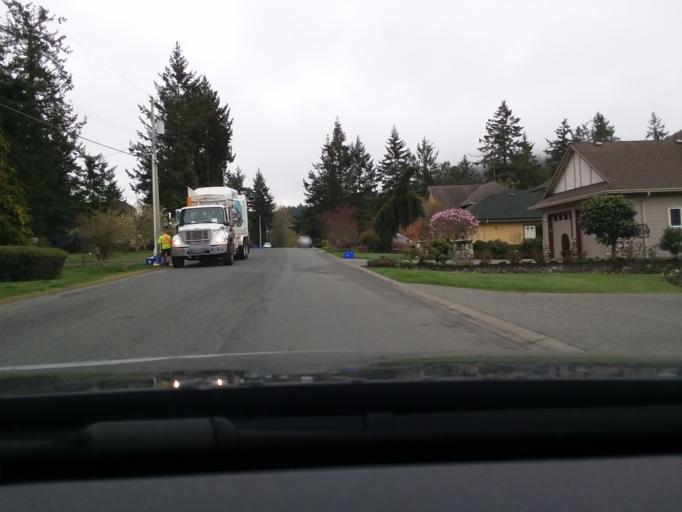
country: CA
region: British Columbia
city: North Saanich
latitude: 48.5531
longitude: -123.4009
